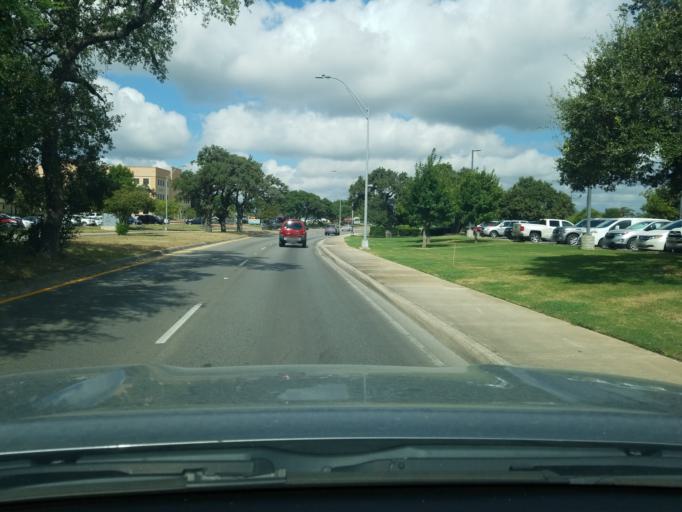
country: US
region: Texas
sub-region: Bexar County
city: Hollywood Park
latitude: 29.6145
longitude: -98.4758
